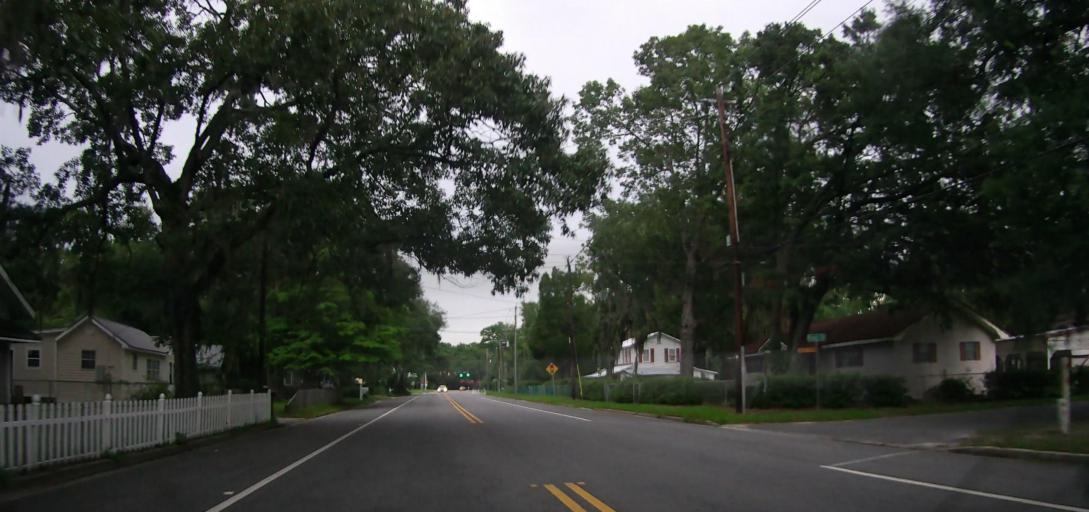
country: US
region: Georgia
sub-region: Glynn County
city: Dock Junction
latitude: 31.2106
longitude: -81.5001
